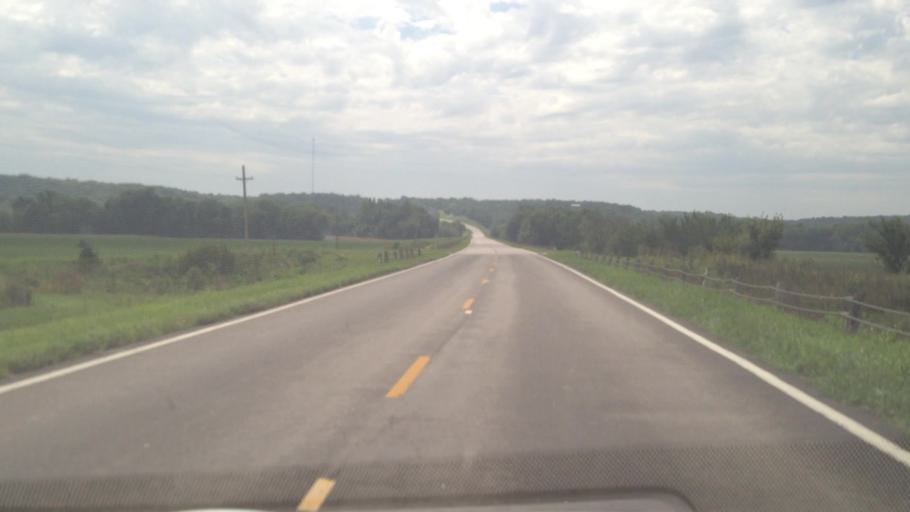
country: US
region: Kansas
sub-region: Bourbon County
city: Fort Scott
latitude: 37.8420
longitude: -94.9813
